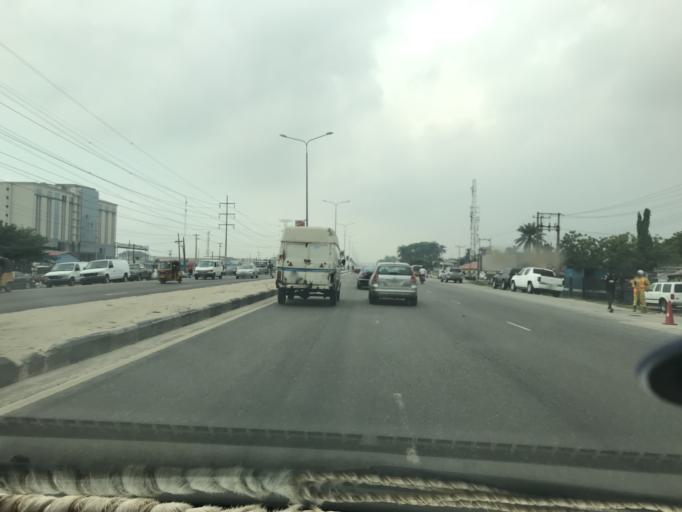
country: NG
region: Lagos
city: Ikoyi
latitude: 6.4496
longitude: 3.5510
